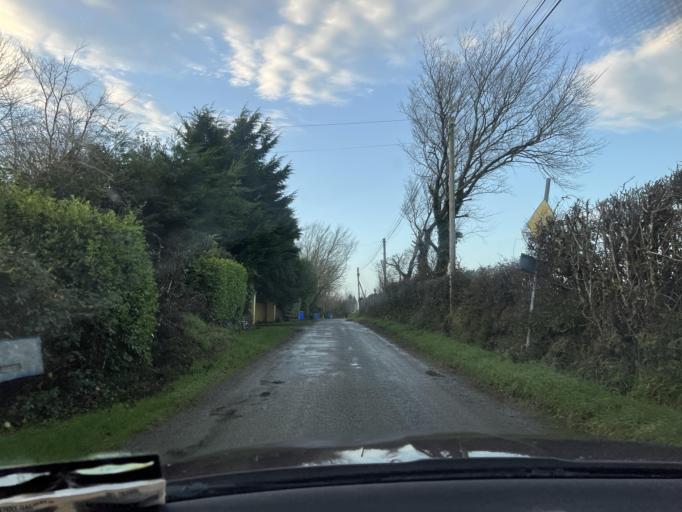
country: IE
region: Leinster
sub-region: Loch Garman
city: Loch Garman
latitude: 52.3636
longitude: -6.5279
